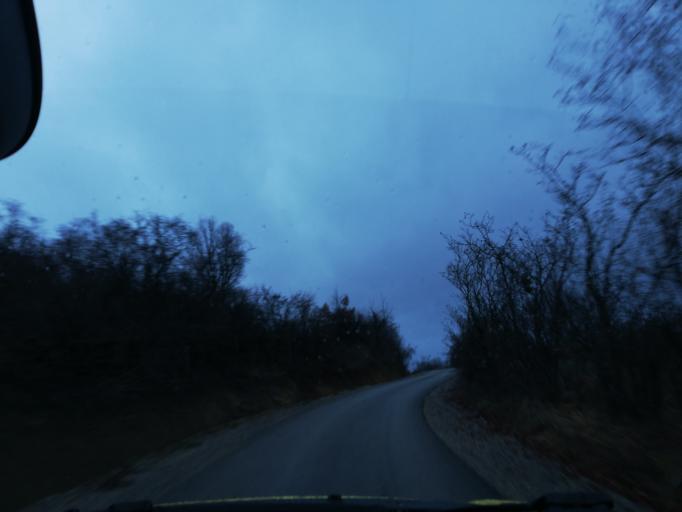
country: RS
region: Central Serbia
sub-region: Pirotski Okrug
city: Dimitrovgrad
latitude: 43.0099
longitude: 22.7186
